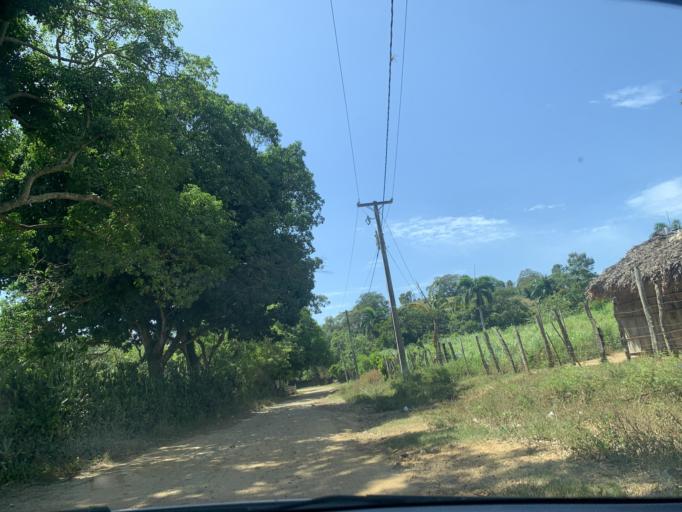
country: DO
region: Puerto Plata
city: Luperon
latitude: 19.8821
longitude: -70.8688
